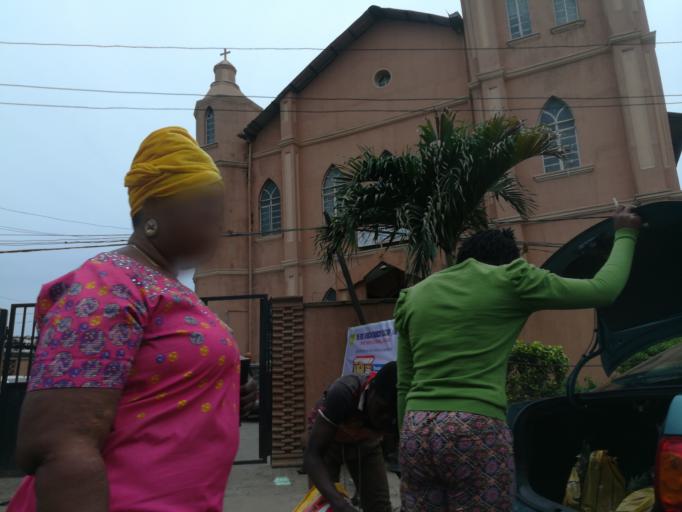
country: NG
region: Lagos
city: Ebute Metta
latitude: 6.4806
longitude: 3.3840
